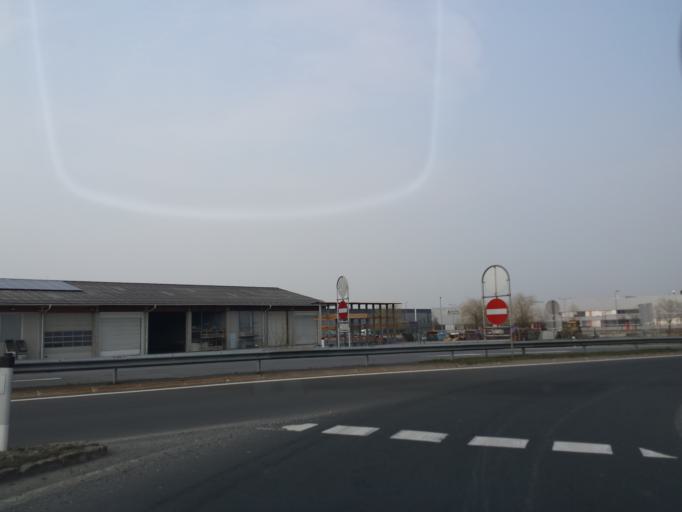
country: AT
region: Styria
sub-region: Politischer Bezirk Hartberg-Fuerstenfeld
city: Ilz
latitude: 47.0814
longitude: 15.9594
